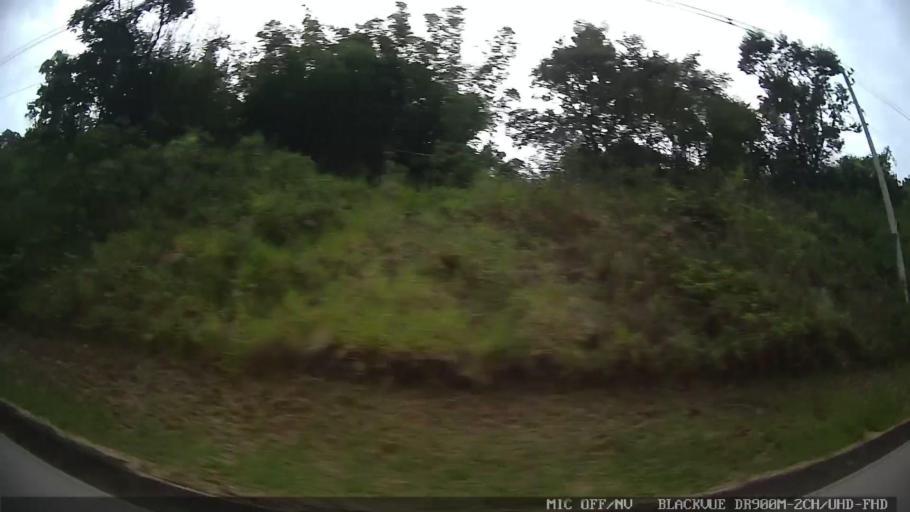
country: BR
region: Sao Paulo
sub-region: Caraguatatuba
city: Caraguatatuba
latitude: -23.4730
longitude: -45.5849
